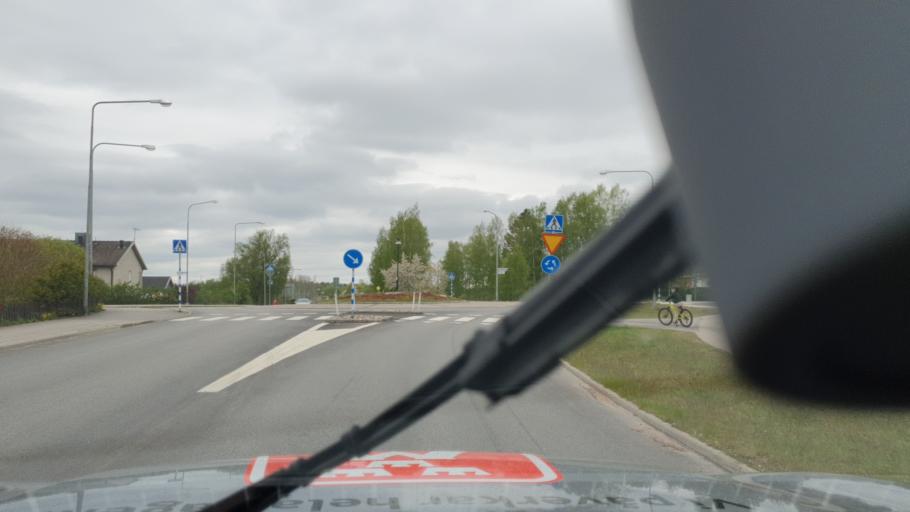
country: SE
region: Kalmar
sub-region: Vimmerby Kommun
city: Vimmerby
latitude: 57.6751
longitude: 15.8681
